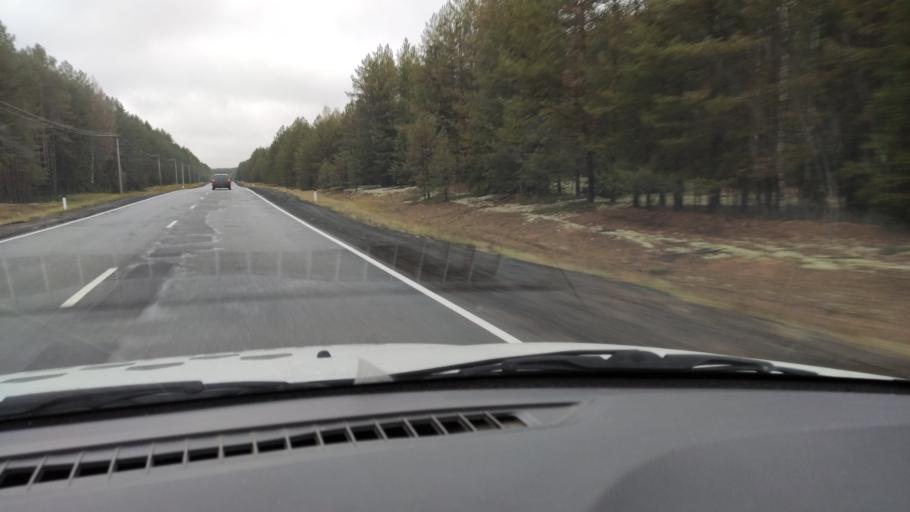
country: RU
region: Kirov
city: Belaya Kholunitsa
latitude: 58.9073
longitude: 51.0071
